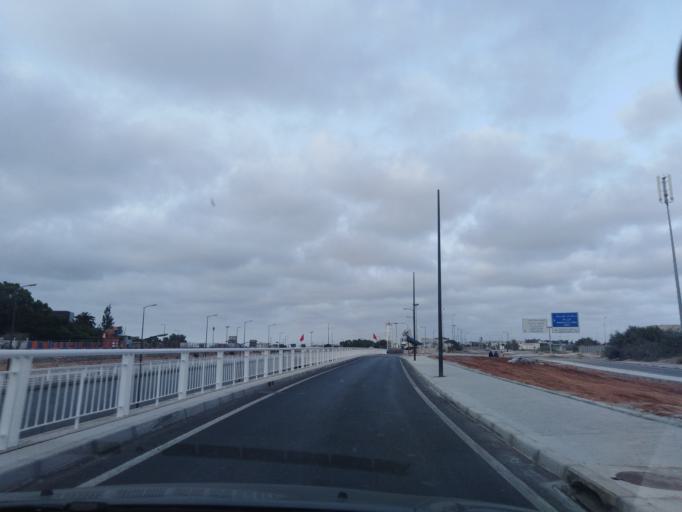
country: MA
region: Grand Casablanca
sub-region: Casablanca
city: Casablanca
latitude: 33.5455
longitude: -7.6500
